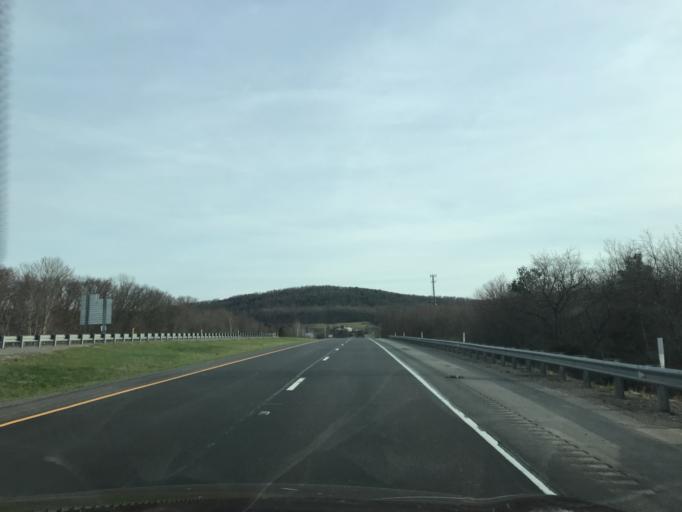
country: US
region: Pennsylvania
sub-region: Lycoming County
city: Muncy
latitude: 41.2016
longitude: -76.7691
